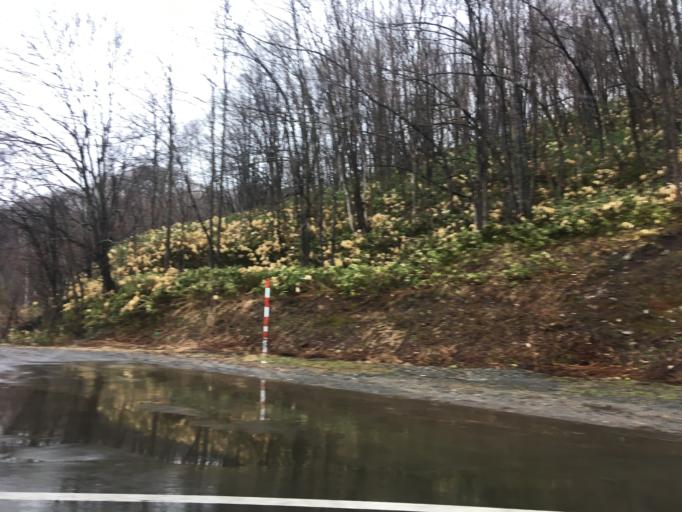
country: JP
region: Hokkaido
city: Nayoro
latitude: 44.0798
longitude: 142.4198
